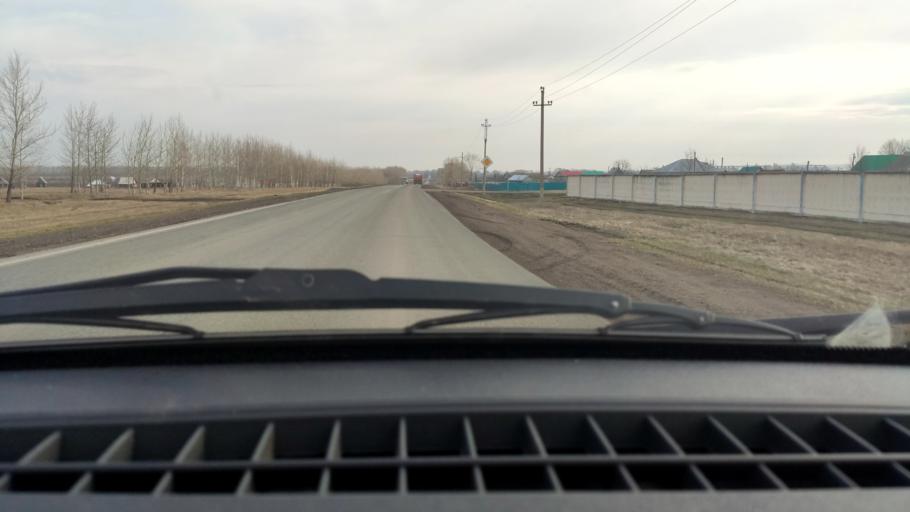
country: RU
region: Bashkortostan
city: Davlekanovo
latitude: 54.3850
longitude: 55.1976
